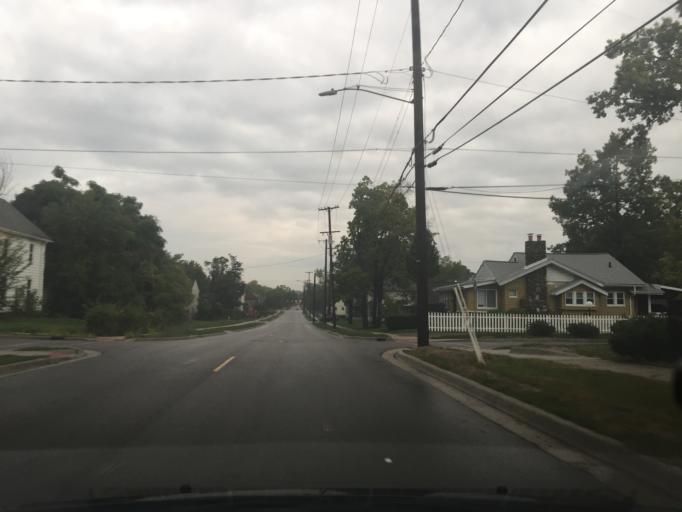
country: US
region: Michigan
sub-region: Oakland County
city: Pontiac
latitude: 42.6313
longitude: -83.2821
